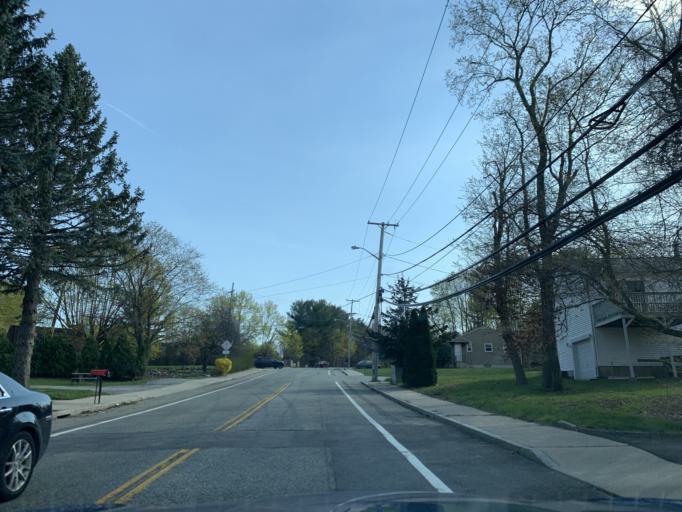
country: US
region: Rhode Island
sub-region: Providence County
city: Johnston
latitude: 41.8059
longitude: -71.4938
